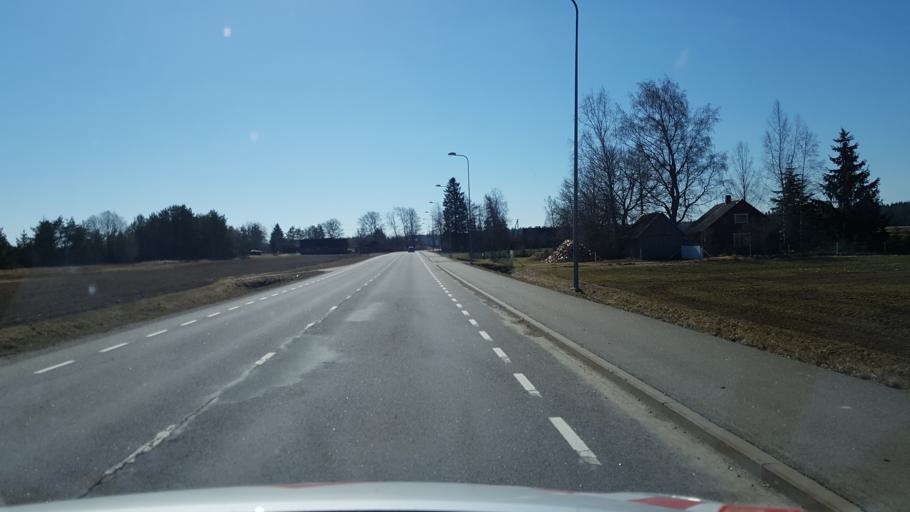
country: EE
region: Laeaene-Virumaa
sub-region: Vinni vald
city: Vinni
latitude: 59.1524
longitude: 26.5922
